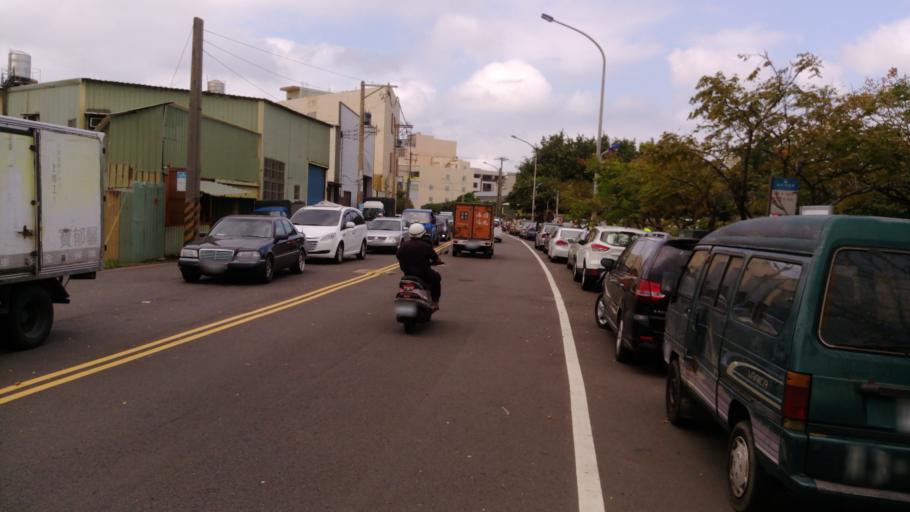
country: TW
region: Taiwan
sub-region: Hsinchu
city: Hsinchu
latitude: 24.7923
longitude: 120.9304
